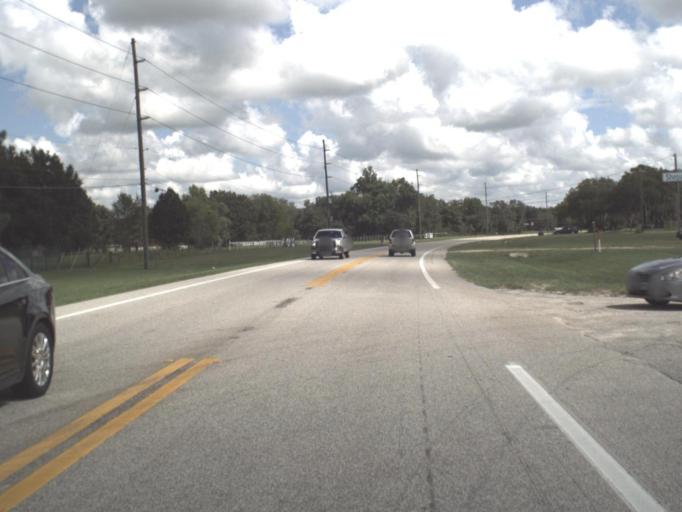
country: US
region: Florida
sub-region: Polk County
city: Polk City
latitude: 28.1738
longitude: -81.8543
